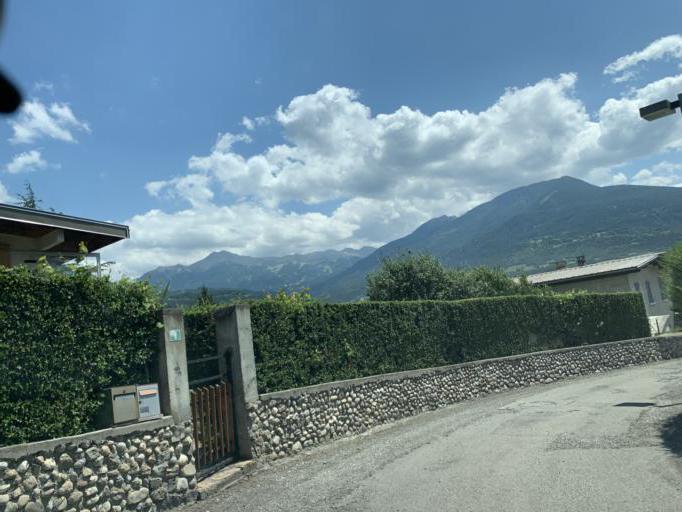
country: FR
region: Provence-Alpes-Cote d'Azur
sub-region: Departement des Hautes-Alpes
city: Embrun
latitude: 44.5542
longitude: 6.4803
